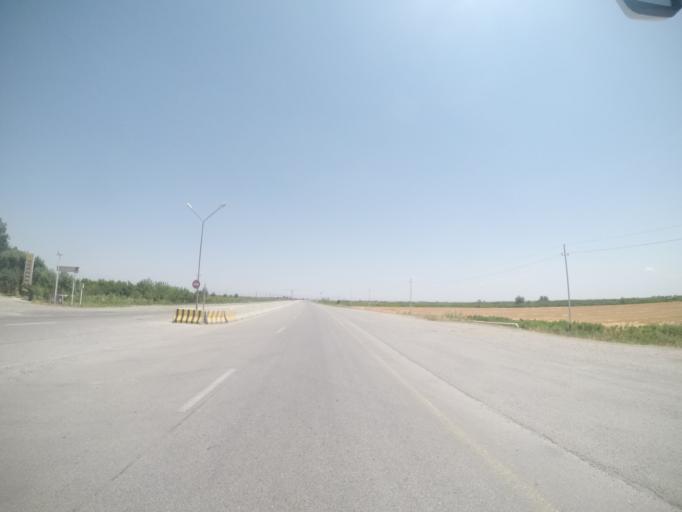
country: AZ
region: Kurdamir Rayon
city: Kyurdarmir
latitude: 40.3155
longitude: 48.1718
